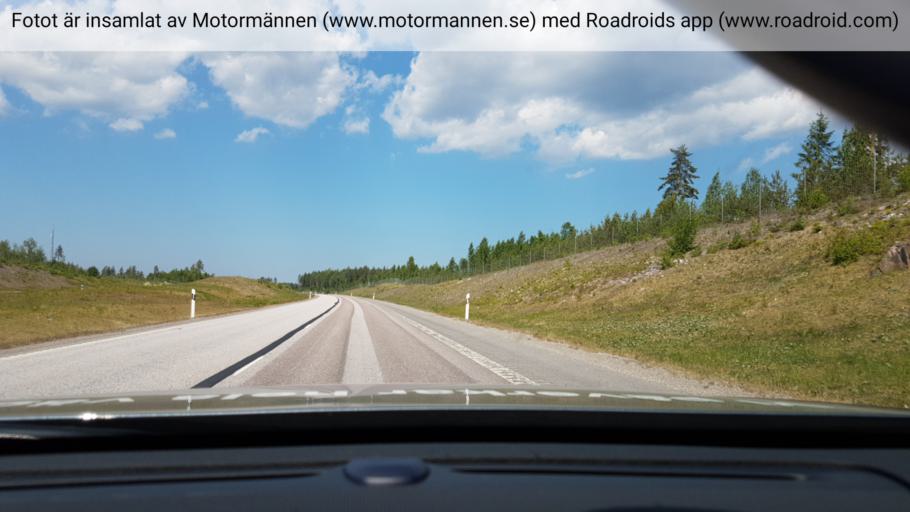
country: SE
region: Uppsala
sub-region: Tierps Kommun
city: Tierp
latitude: 60.3036
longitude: 17.5213
